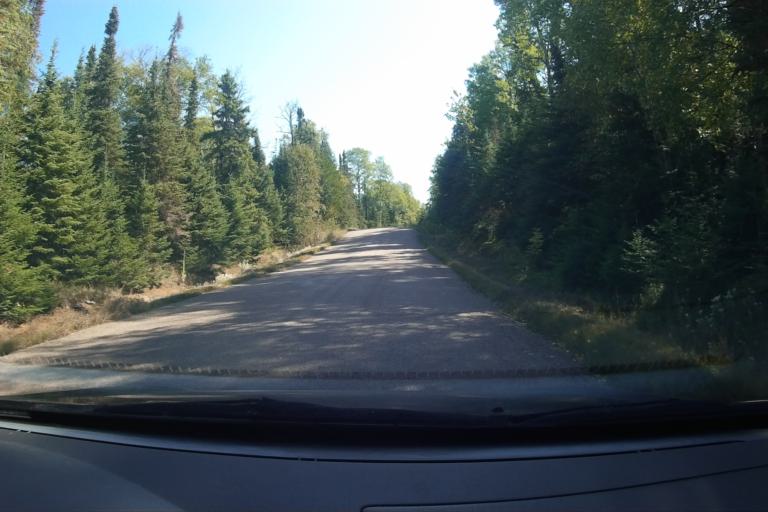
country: CA
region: Ontario
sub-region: Thunder Bay District
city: Thunder Bay
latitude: 48.3476
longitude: -88.8018
